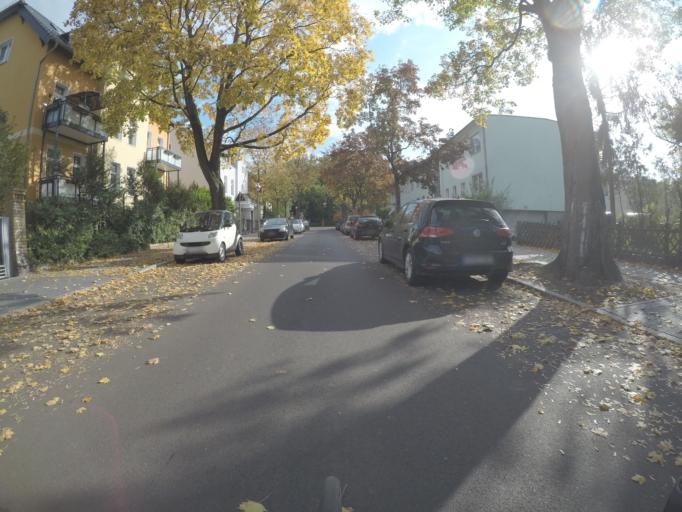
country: DE
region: Berlin
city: Waidmannslust
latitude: 52.6073
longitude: 13.3179
